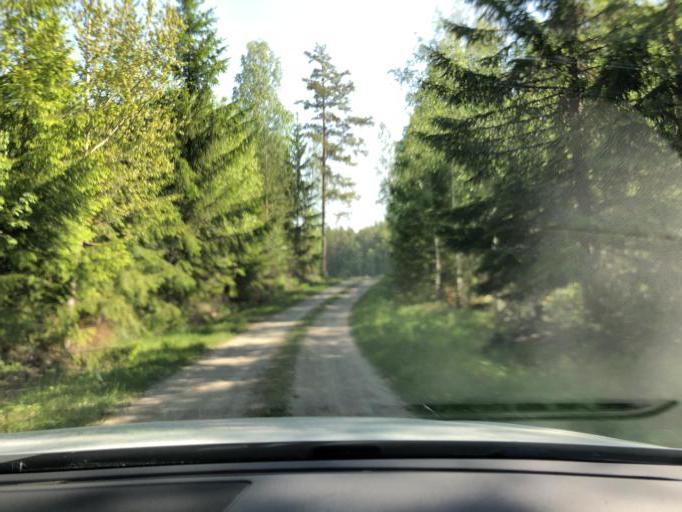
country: SE
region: Dalarna
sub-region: Avesta Kommun
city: Horndal
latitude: 60.2105
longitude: 16.4918
